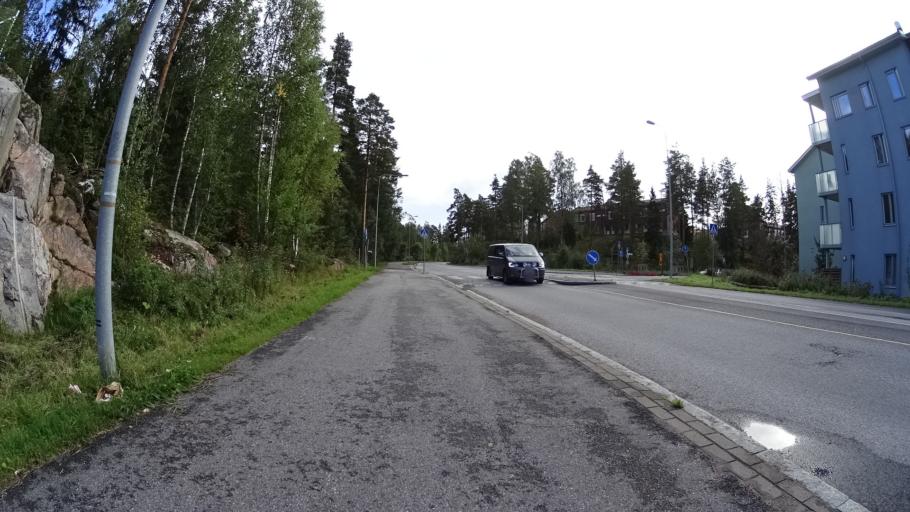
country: FI
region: Uusimaa
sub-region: Helsinki
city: Espoo
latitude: 60.2278
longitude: 24.6671
